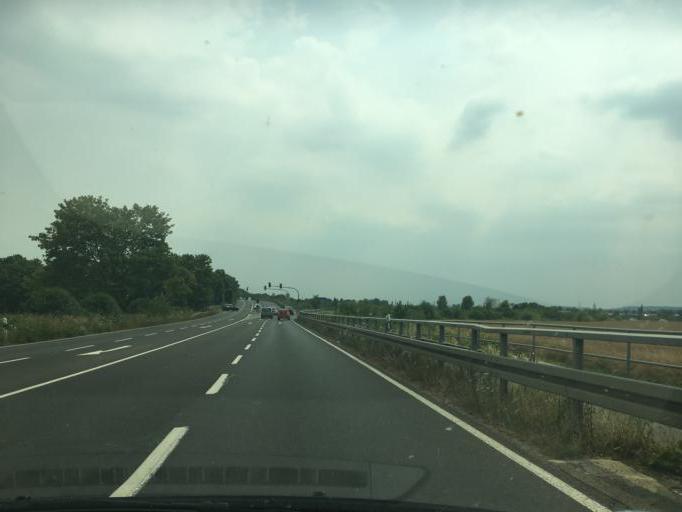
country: DE
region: North Rhine-Westphalia
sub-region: Regierungsbezirk Koln
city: Frechen
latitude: 50.9333
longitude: 6.8163
